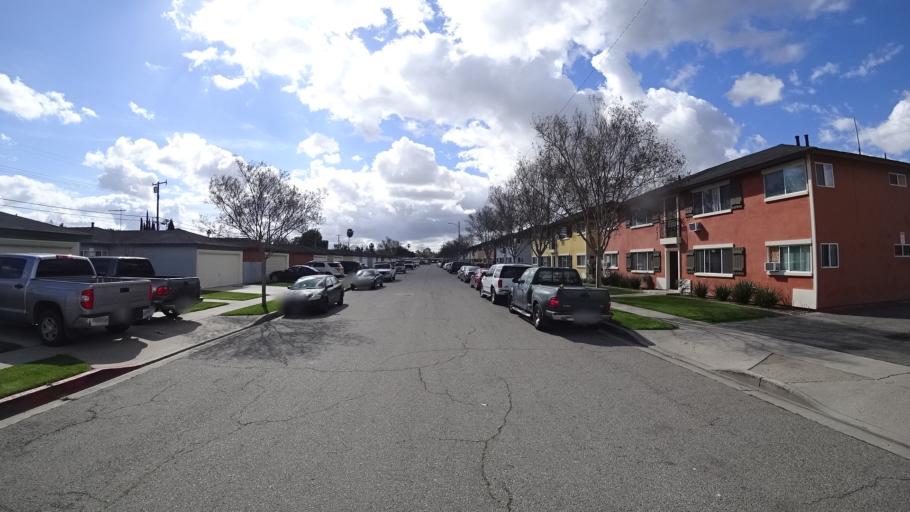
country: US
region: California
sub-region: Orange County
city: Anaheim
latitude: 33.8453
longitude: -117.9085
